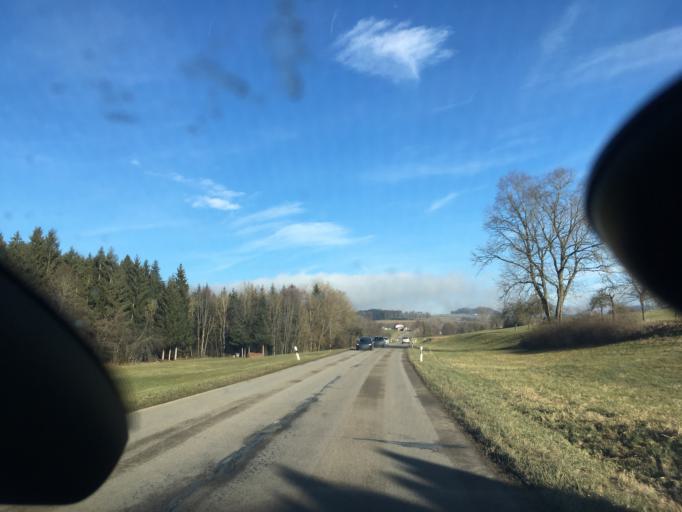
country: DE
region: Baden-Wuerttemberg
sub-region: Freiburg Region
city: Dogern
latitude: 47.6491
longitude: 8.1398
